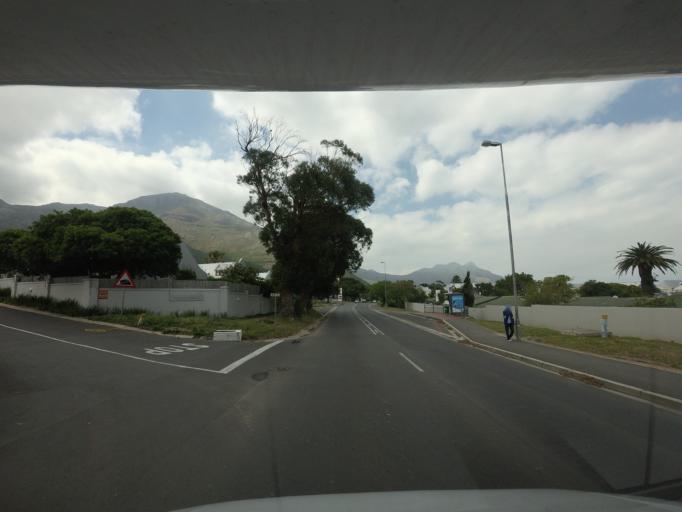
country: ZA
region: Western Cape
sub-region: City of Cape Town
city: Constantia
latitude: -34.0393
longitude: 18.3587
